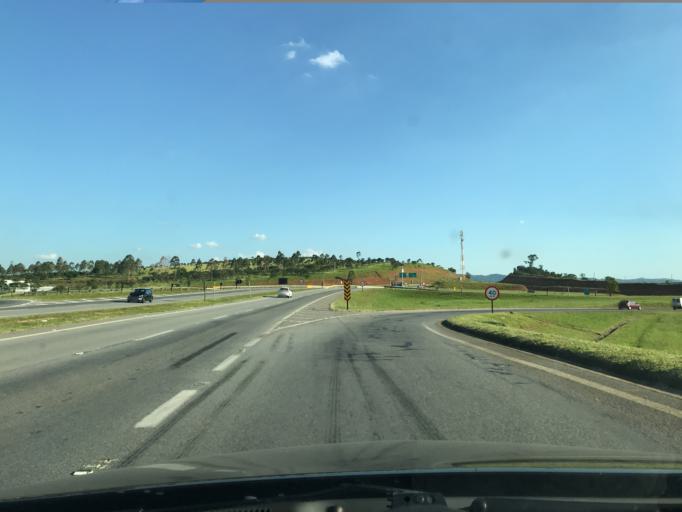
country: BR
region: Sao Paulo
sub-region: Taubate
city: Taubate
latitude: -23.0570
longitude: -45.6215
